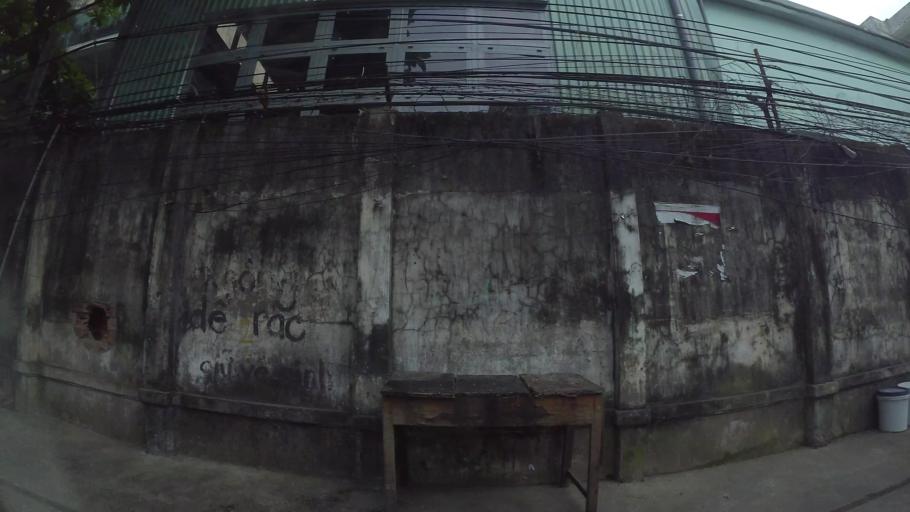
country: VN
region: Da Nang
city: Son Tra
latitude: 16.0604
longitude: 108.2435
